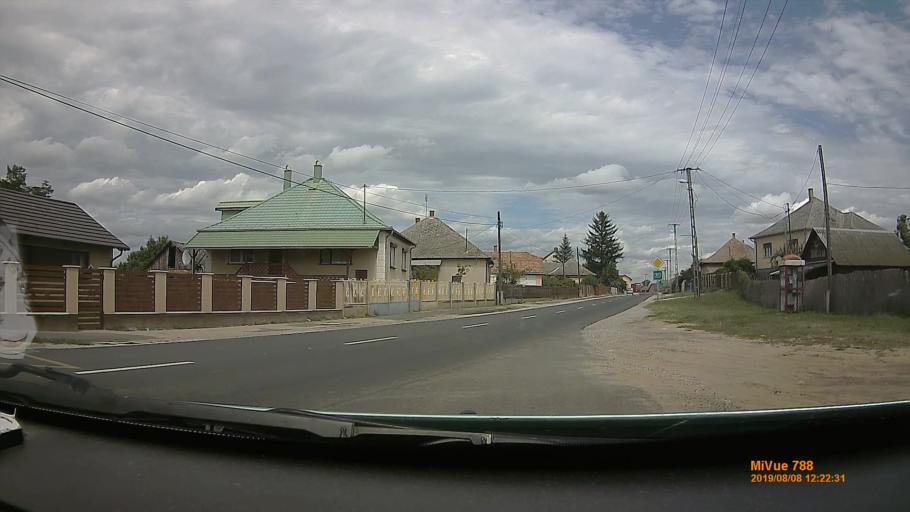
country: HU
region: Szabolcs-Szatmar-Bereg
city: Nyirbogat
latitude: 47.7996
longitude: 22.0538
